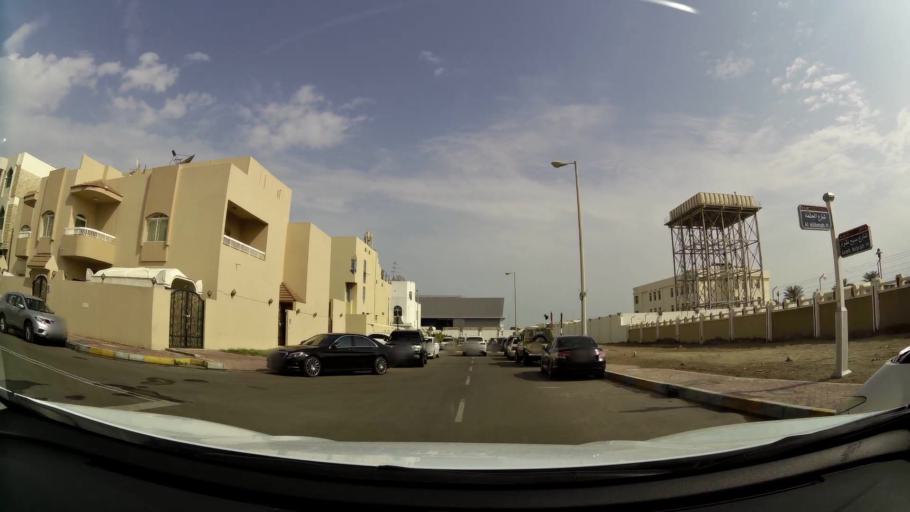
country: AE
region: Abu Dhabi
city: Abu Dhabi
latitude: 24.4392
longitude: 54.4197
